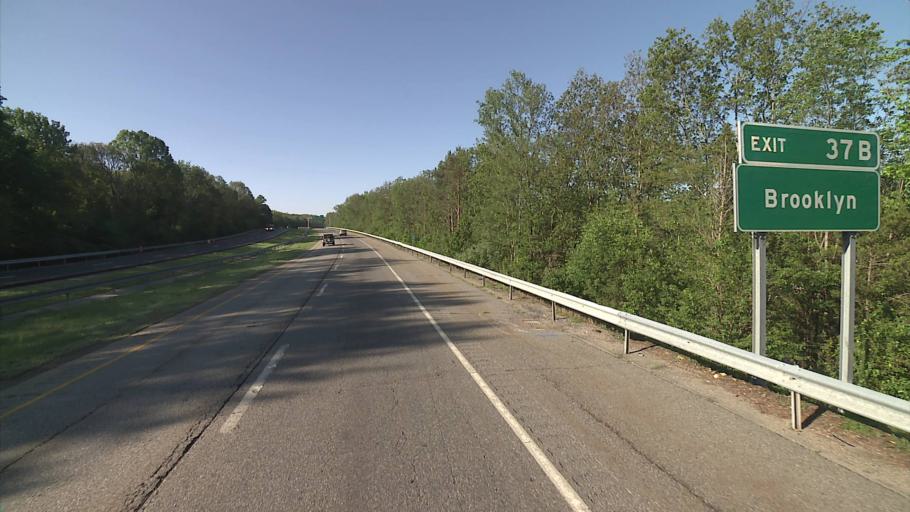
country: US
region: Connecticut
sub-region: Windham County
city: Danielson
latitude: 41.8076
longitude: -71.8728
